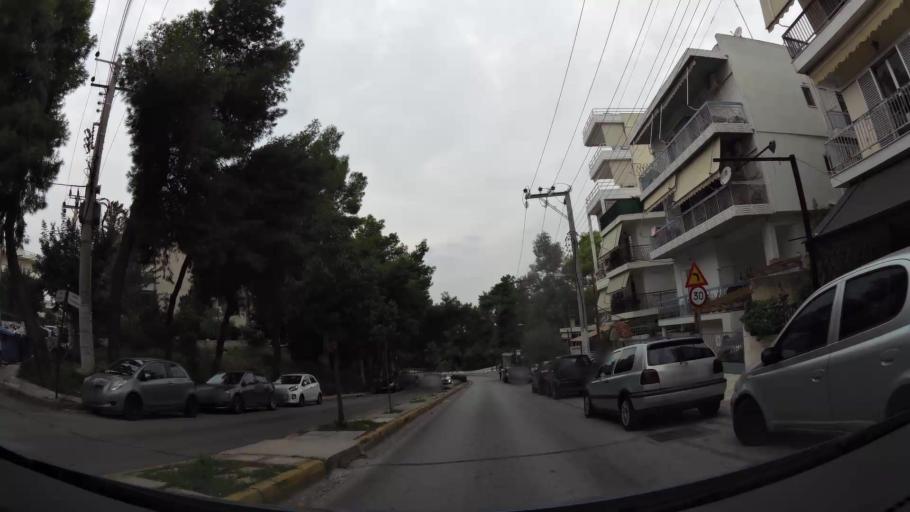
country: GR
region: Attica
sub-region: Nomarchia Athinas
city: Alimos
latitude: 37.9139
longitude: 23.7272
